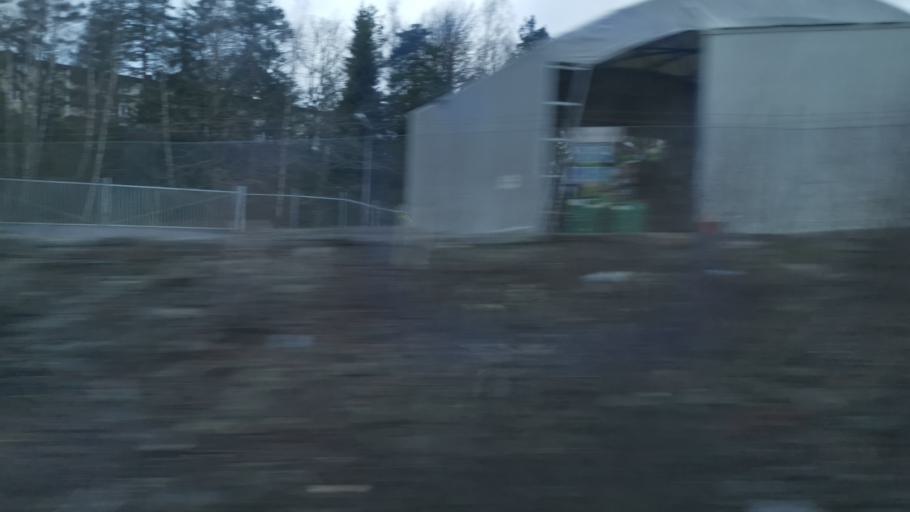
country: SE
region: Stockholm
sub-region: Sodertalje Kommun
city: Pershagen
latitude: 59.0971
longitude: 17.5780
